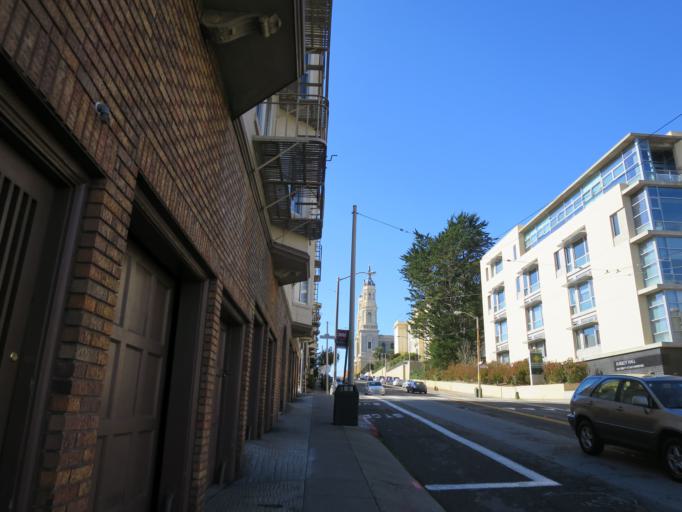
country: US
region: California
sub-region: San Francisco County
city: San Francisco
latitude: 37.7754
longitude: -122.4492
